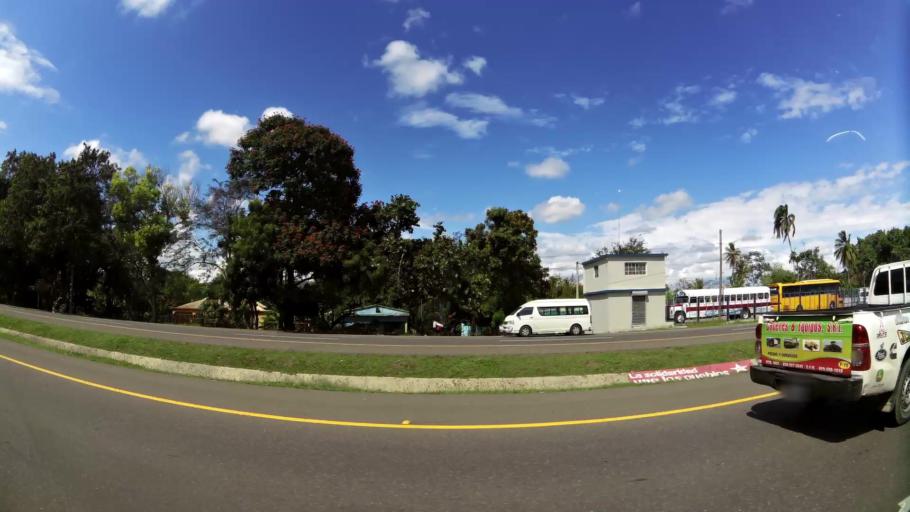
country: DO
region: La Vega
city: Concepcion de La Vega
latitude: 19.2469
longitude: -70.5451
